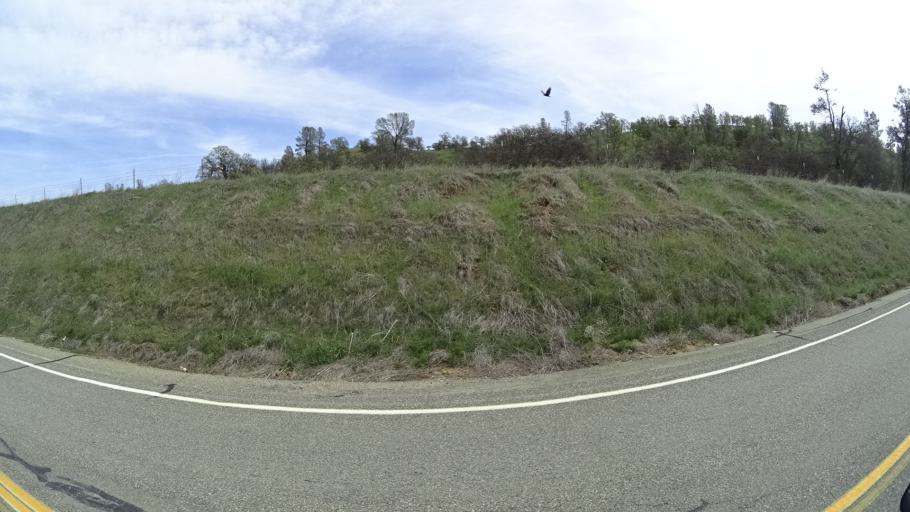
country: US
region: California
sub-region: Glenn County
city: Willows
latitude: 39.5788
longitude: -122.5403
